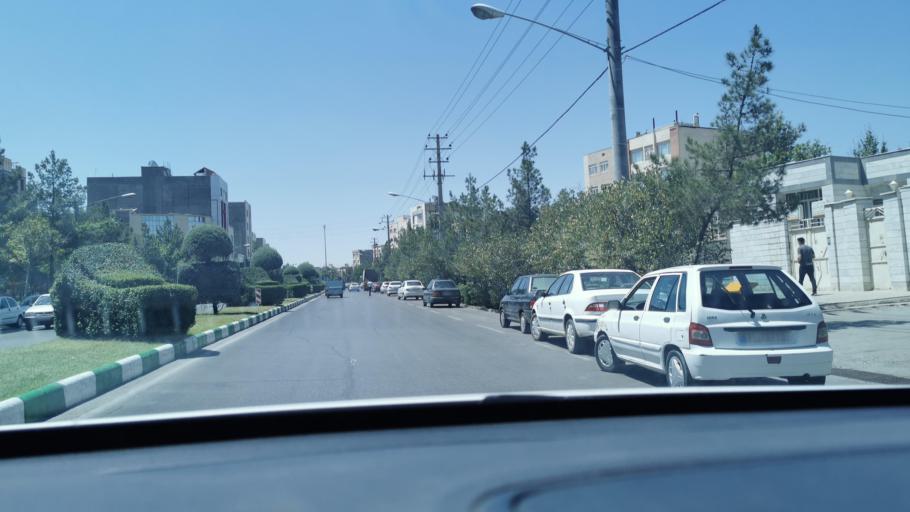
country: IR
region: Razavi Khorasan
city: Mashhad
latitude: 36.3389
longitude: 59.4857
